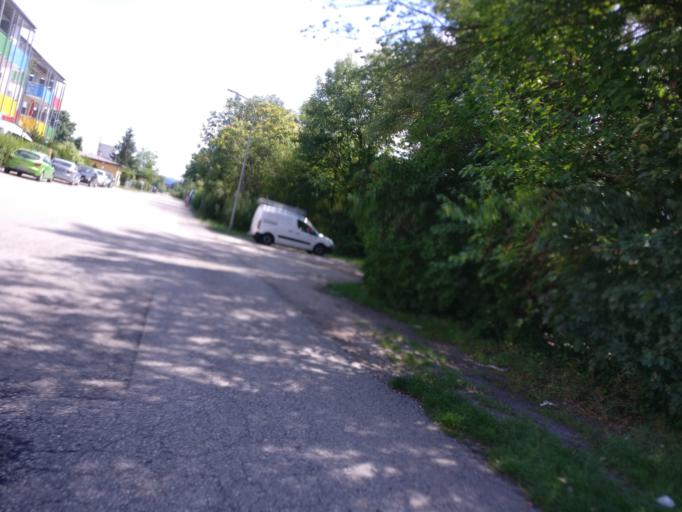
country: AT
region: Lower Austria
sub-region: Politischer Bezirk Neunkirchen
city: Neunkirchen
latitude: 47.7242
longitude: 16.0943
